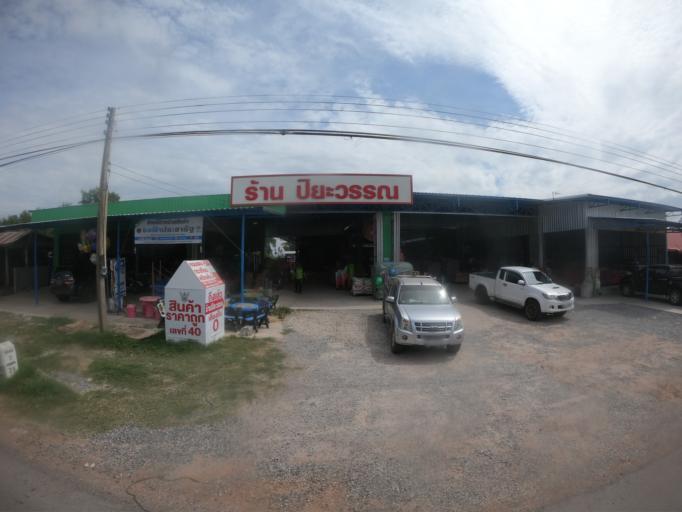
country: TH
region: Maha Sarakham
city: Chiang Yuen
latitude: 16.3989
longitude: 103.1001
